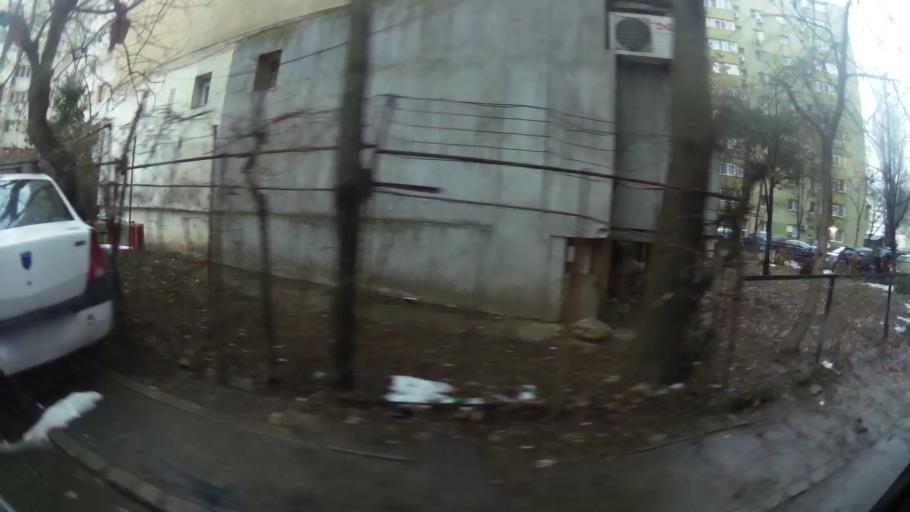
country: RO
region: Ilfov
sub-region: Comuna Chiajna
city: Rosu
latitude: 44.4328
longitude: 26.0236
